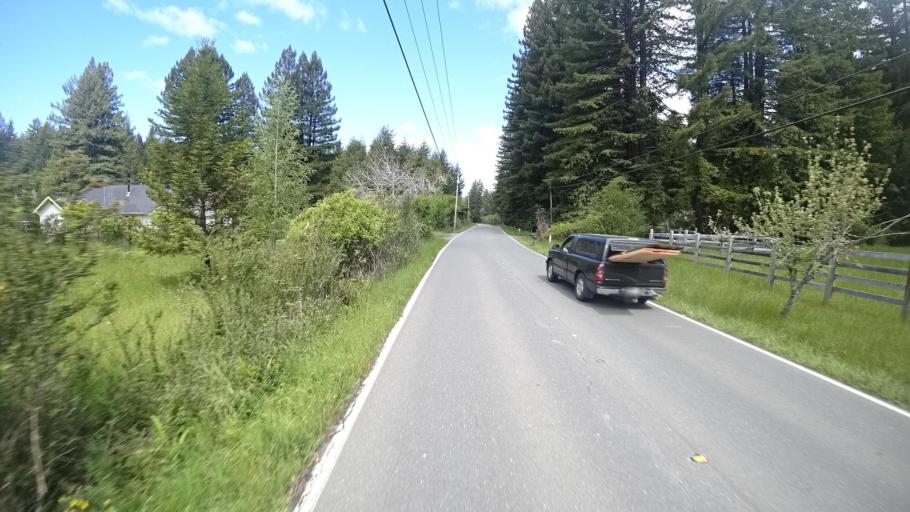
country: US
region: California
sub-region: Humboldt County
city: McKinleyville
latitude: 40.9437
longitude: -124.0273
